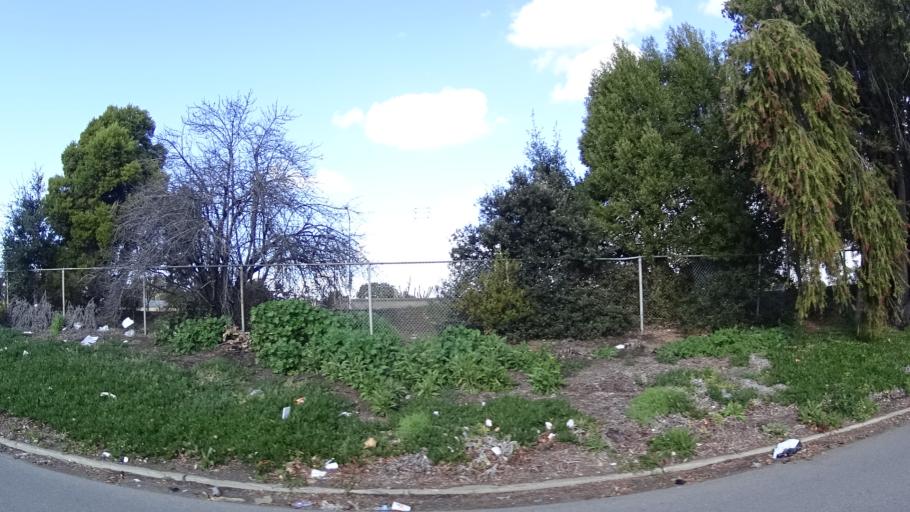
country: US
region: California
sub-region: Alameda County
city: Cherryland
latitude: 37.6554
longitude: -122.1035
